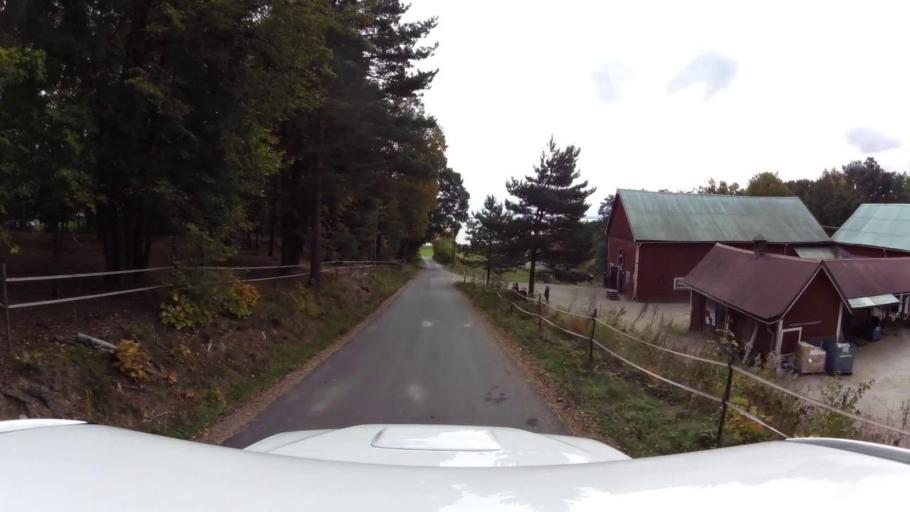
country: SE
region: OEstergoetland
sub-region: Linkopings Kommun
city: Berg
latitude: 58.5127
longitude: 15.5516
